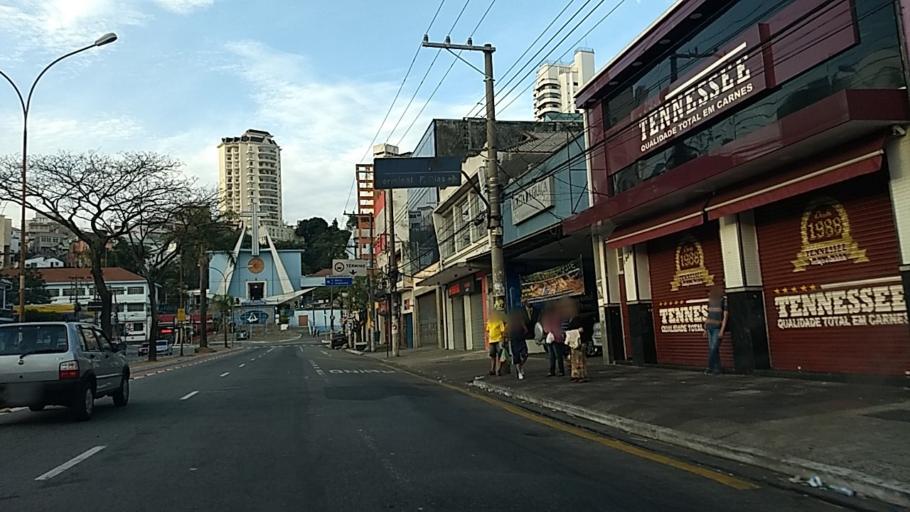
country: BR
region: Sao Paulo
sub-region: Sao Paulo
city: Sao Paulo
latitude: -23.5135
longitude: -46.5858
